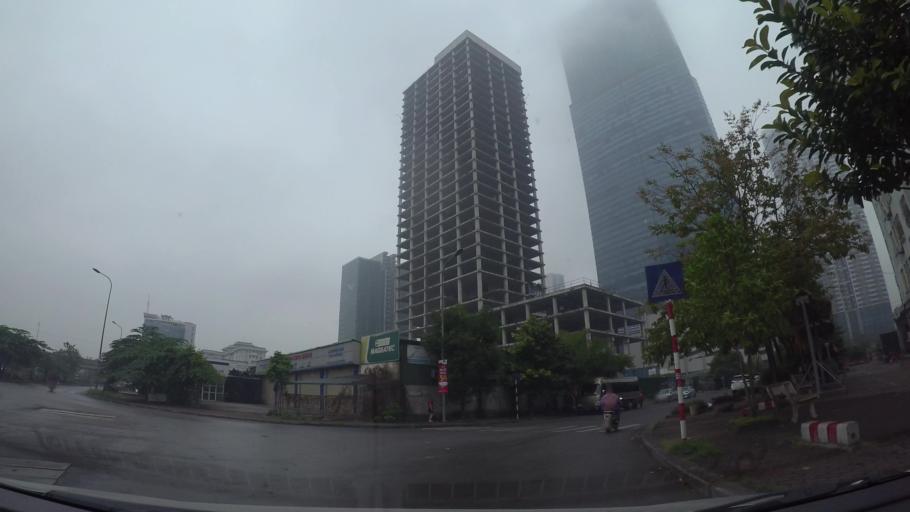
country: VN
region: Ha Noi
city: Cau Giay
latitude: 21.0153
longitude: 105.7863
